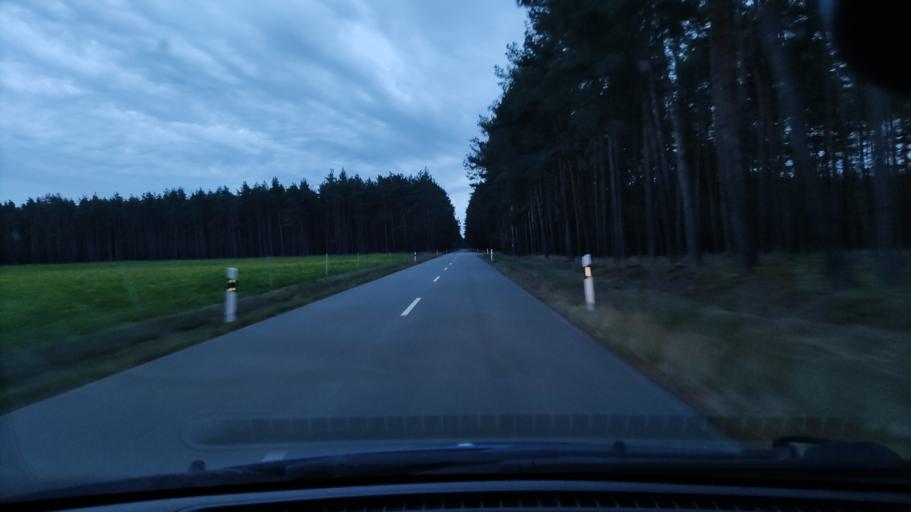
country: DE
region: Lower Saxony
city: Gorleben
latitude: 53.0297
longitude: 11.3854
